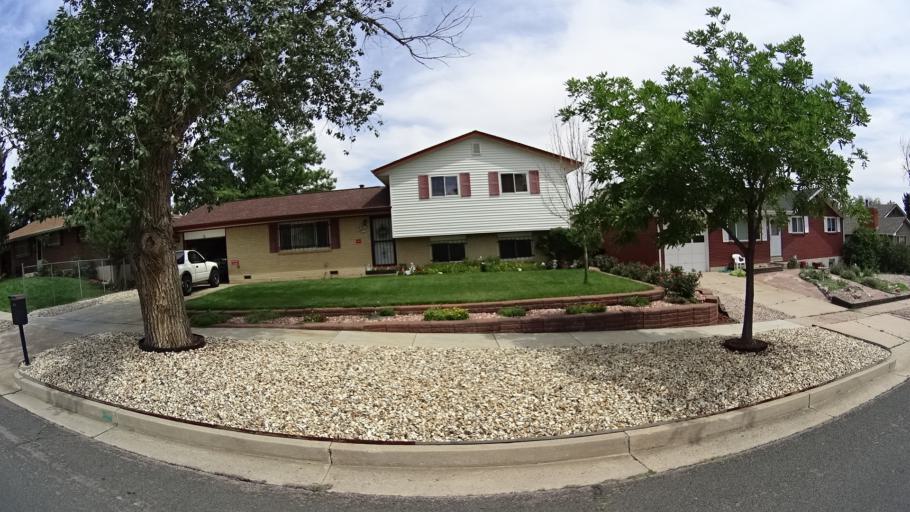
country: US
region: Colorado
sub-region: El Paso County
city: Colorado Springs
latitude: 38.8853
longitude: -104.8367
